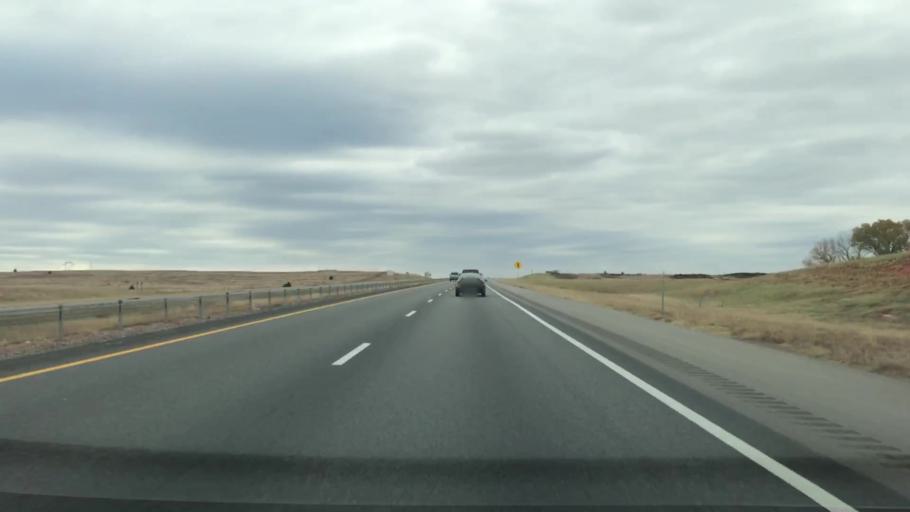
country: US
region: Oklahoma
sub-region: Beckham County
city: Elk City
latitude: 35.3858
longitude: -99.4704
